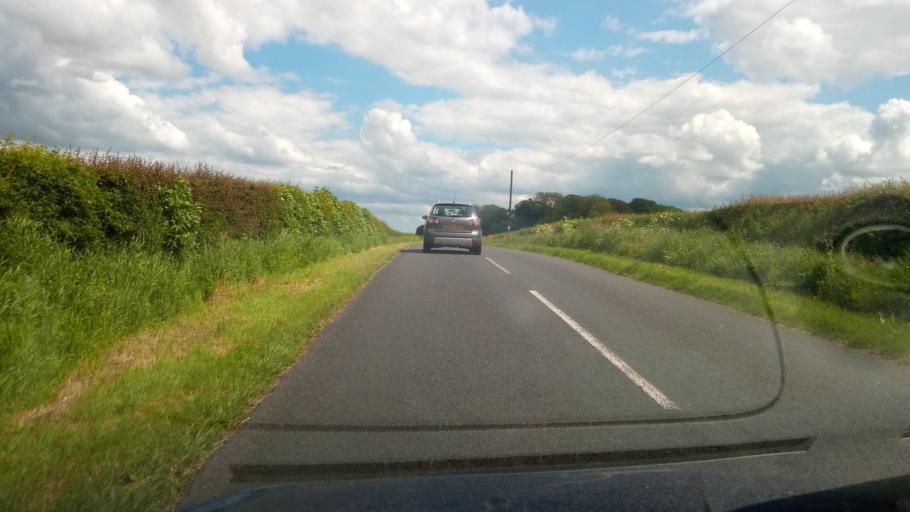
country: GB
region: Scotland
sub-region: The Scottish Borders
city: Coldstream
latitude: 55.6049
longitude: -2.3120
